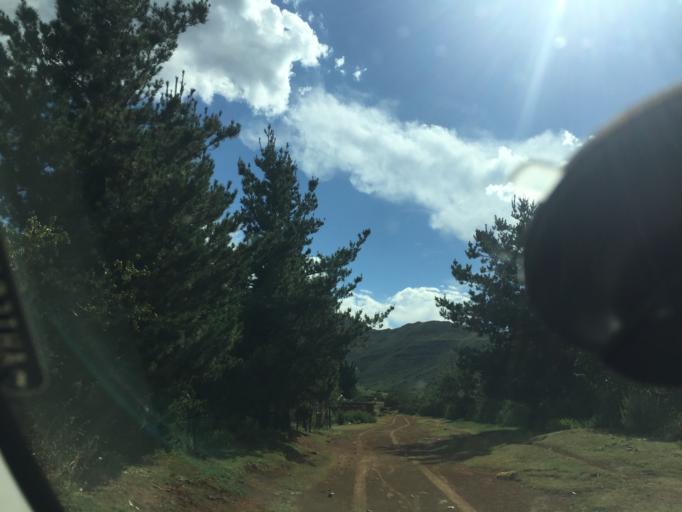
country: LS
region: Maseru
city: Nako
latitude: -29.5900
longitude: 27.7561
